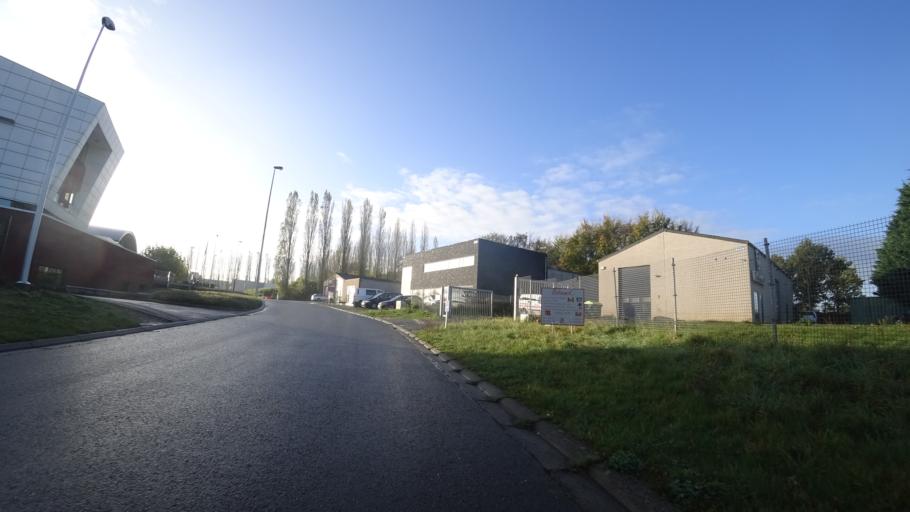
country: BE
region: Wallonia
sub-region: Province de Namur
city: Floreffe
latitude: 50.4910
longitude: 4.7910
